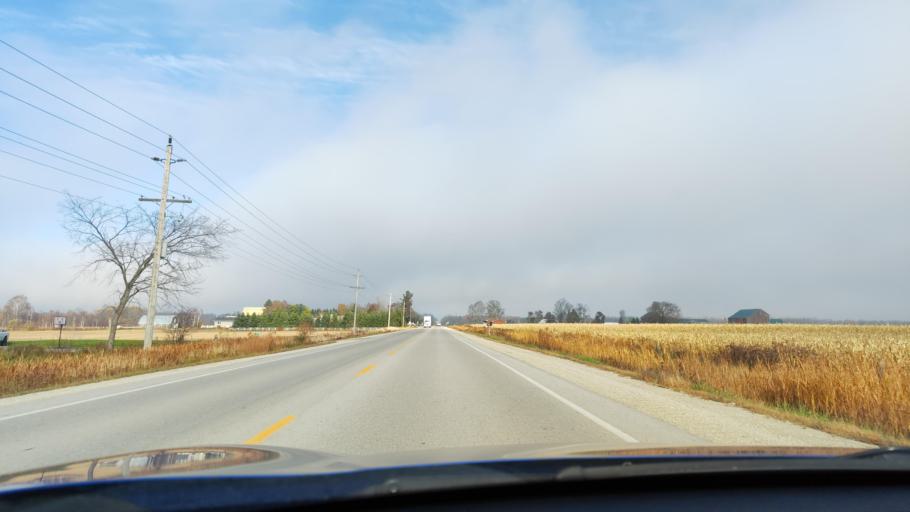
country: CA
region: Ontario
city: Wasaga Beach
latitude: 44.4521
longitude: -80.0705
